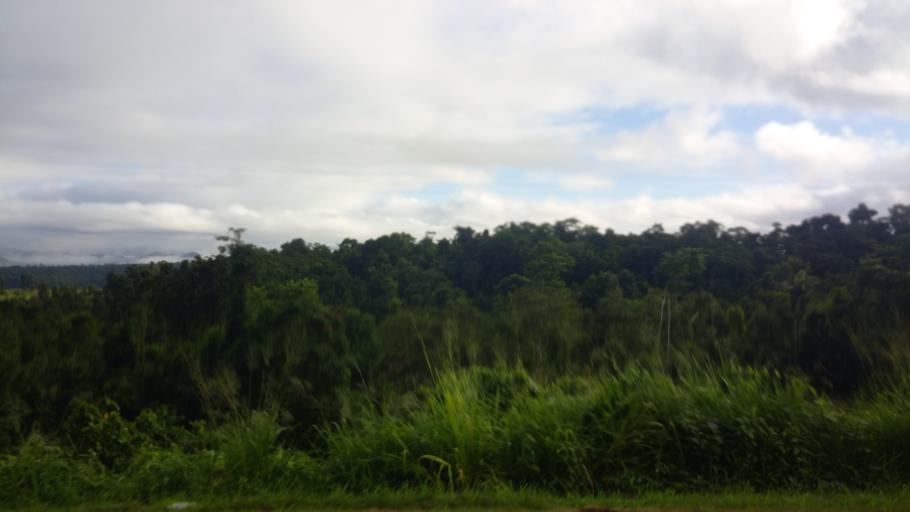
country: AU
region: Queensland
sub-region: Cassowary Coast
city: Innisfail
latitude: -17.5593
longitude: 145.9541
